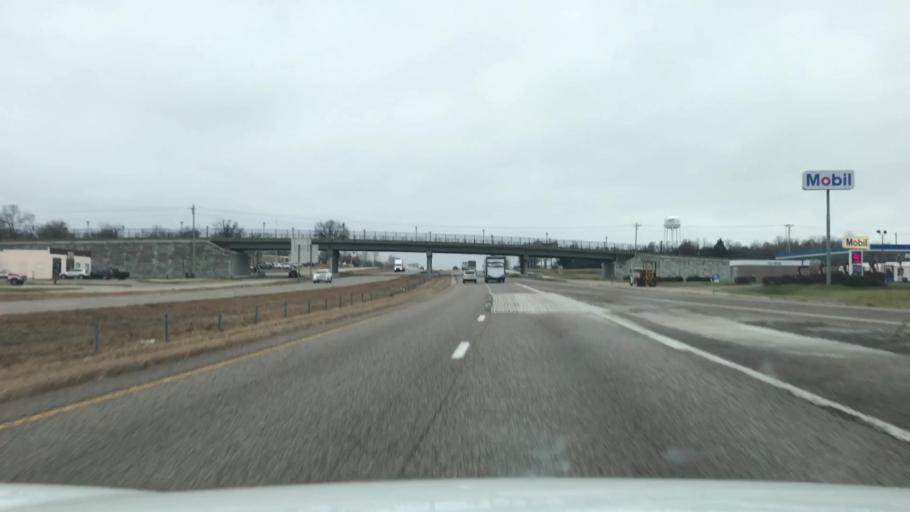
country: US
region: Missouri
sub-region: Franklin County
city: Sullivan
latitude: 38.2099
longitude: -91.1740
